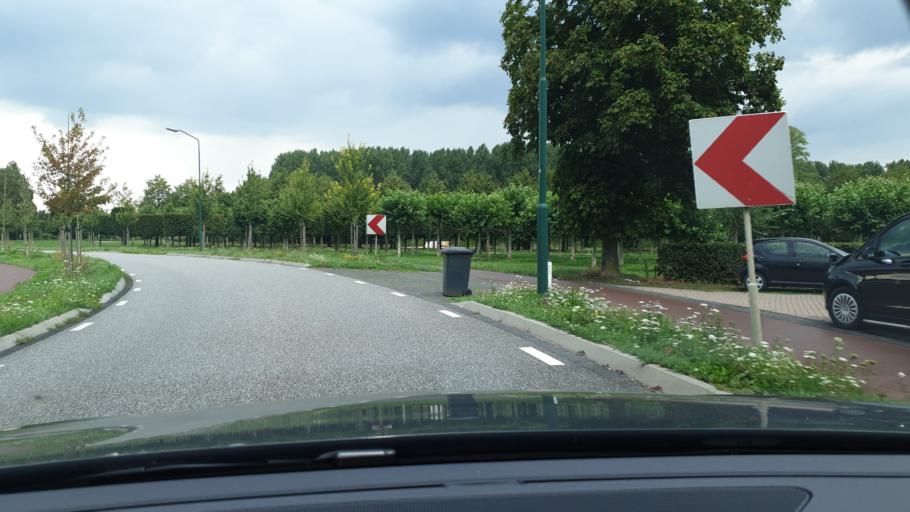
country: NL
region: North Brabant
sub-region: Gemeente Best
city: Best
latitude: 51.5431
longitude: 5.4177
